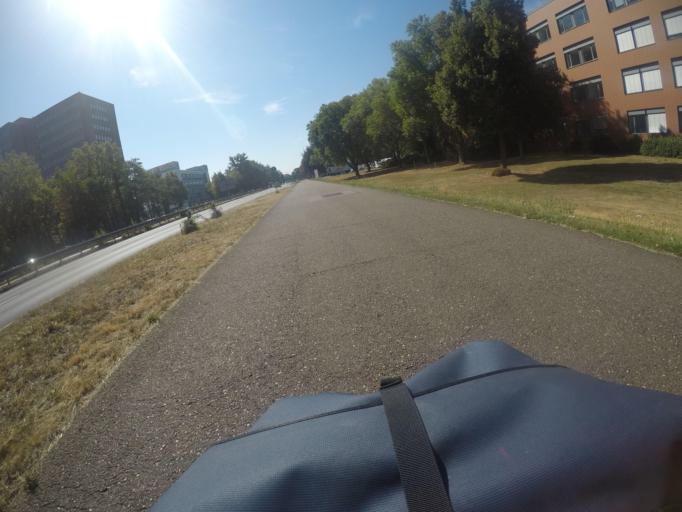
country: DE
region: North Rhine-Westphalia
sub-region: Regierungsbezirk Koln
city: Leverkusen
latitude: 51.0090
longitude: 6.9937
